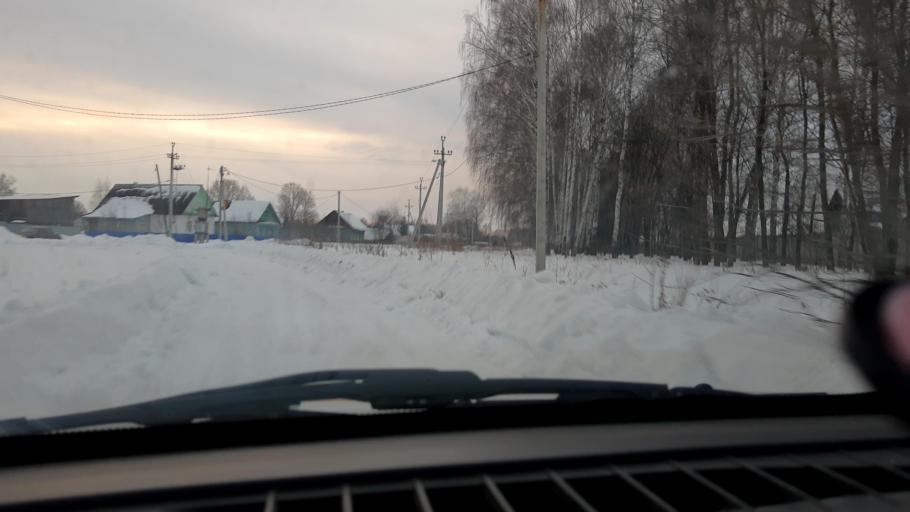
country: RU
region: Bashkortostan
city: Urman
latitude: 54.8737
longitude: 56.8644
